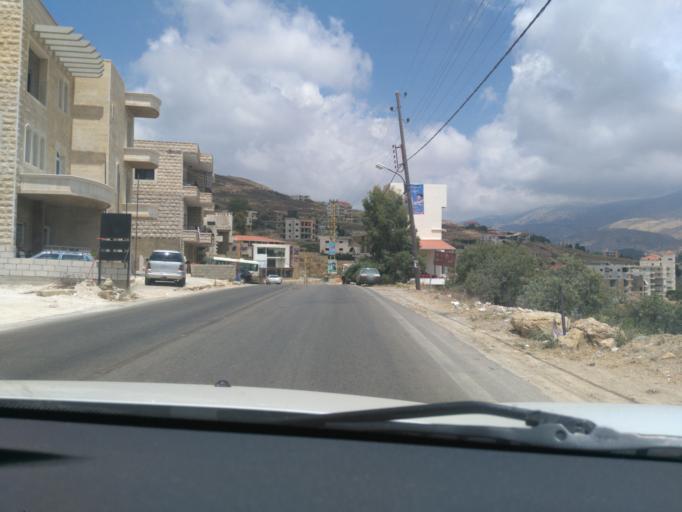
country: LB
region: Mont-Liban
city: Beit ed Dine
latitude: 33.7031
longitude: 35.6628
